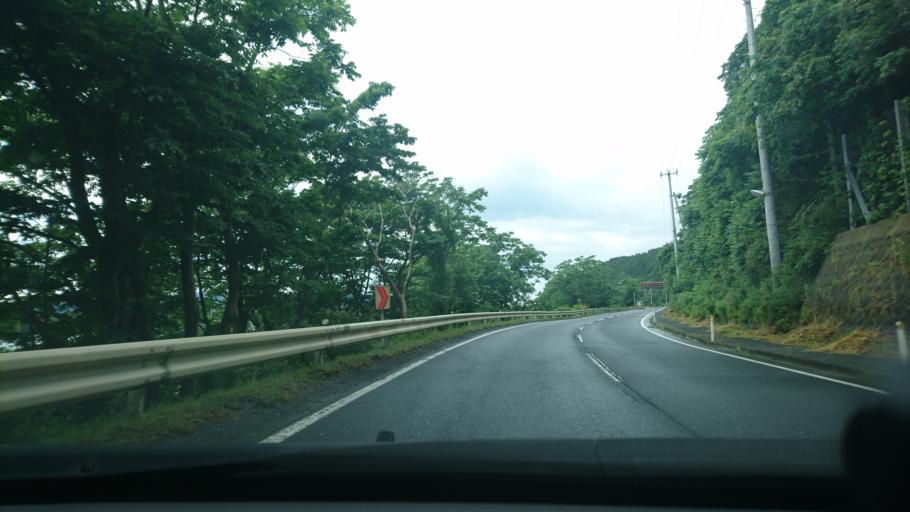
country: JP
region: Miyagi
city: Wakuya
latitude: 38.5960
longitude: 141.3040
